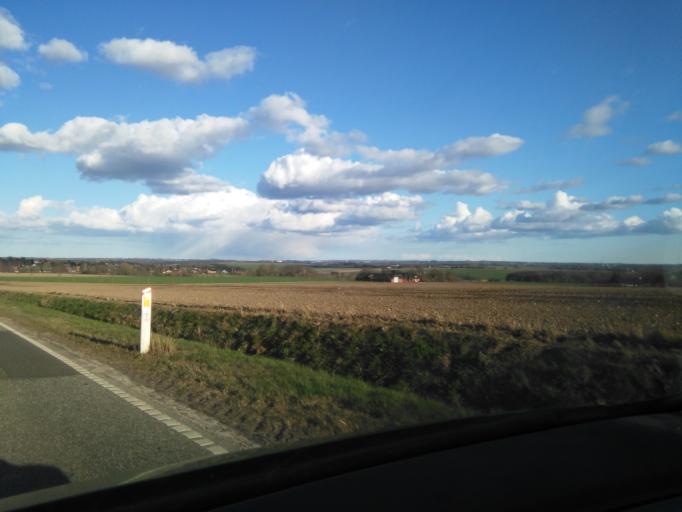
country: DK
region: Central Jutland
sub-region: Skanderborg Kommune
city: Skovby
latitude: 56.1838
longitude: 9.9486
